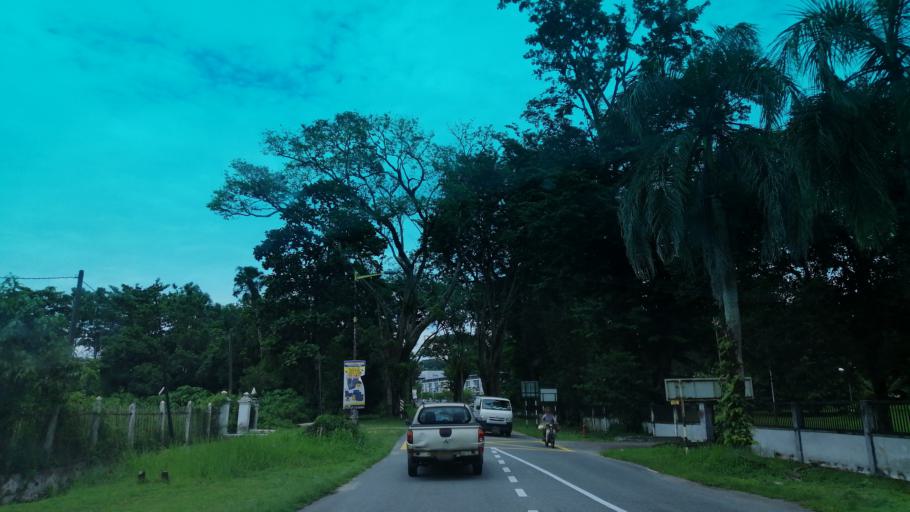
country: MY
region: Perak
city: Taiping
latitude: 4.8581
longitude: 100.7387
